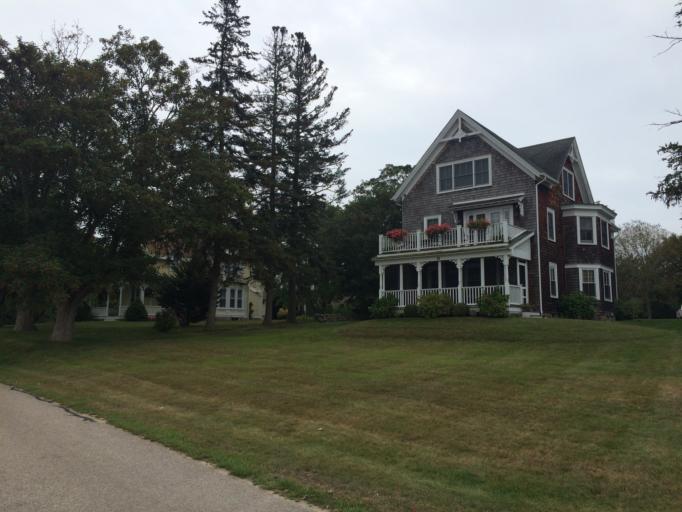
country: US
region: Connecticut
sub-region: New London County
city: Pawcatuck
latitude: 41.3319
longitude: -71.8401
